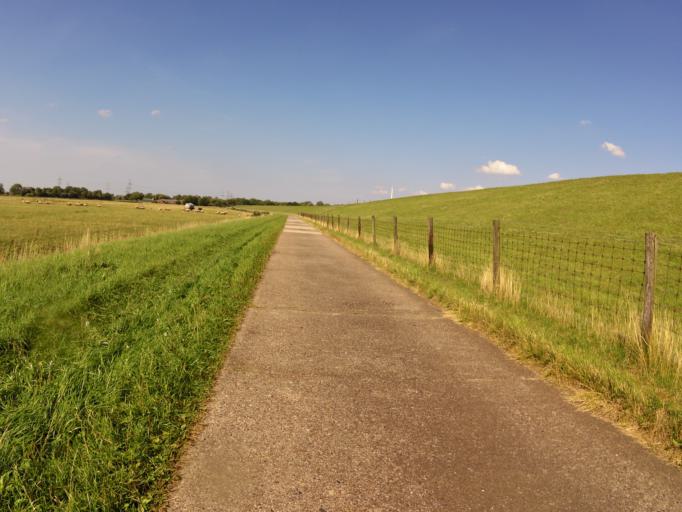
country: DE
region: Lower Saxony
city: Nordenham
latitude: 53.4175
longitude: 8.4723
